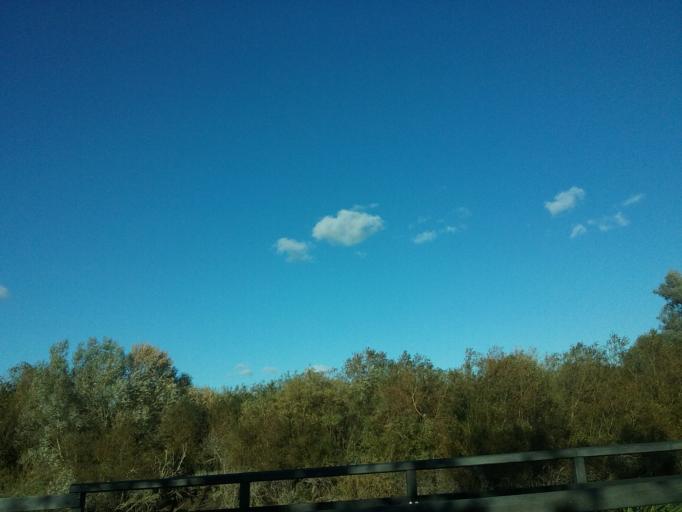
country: IE
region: Leinster
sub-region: Lu
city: Tullyallen
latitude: 53.7187
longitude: -6.4038
